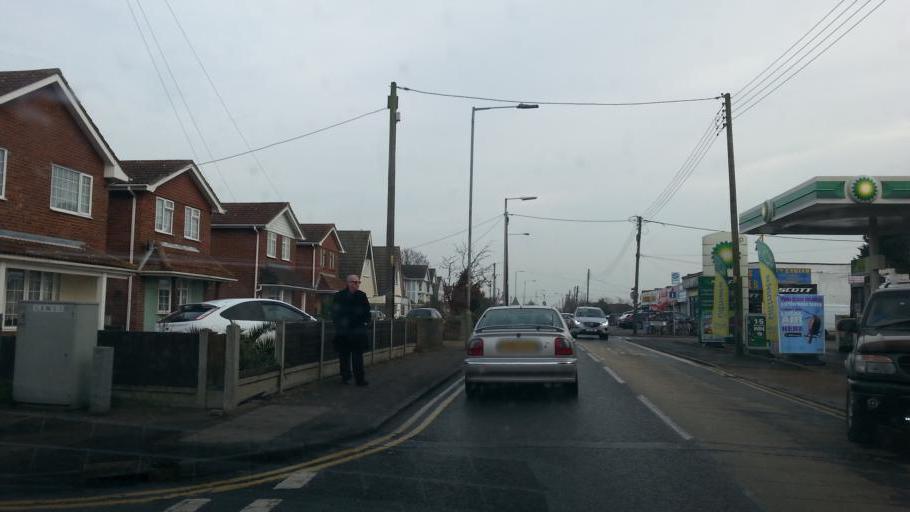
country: GB
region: England
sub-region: Essex
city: Canvey Island
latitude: 51.5198
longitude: 0.5672
